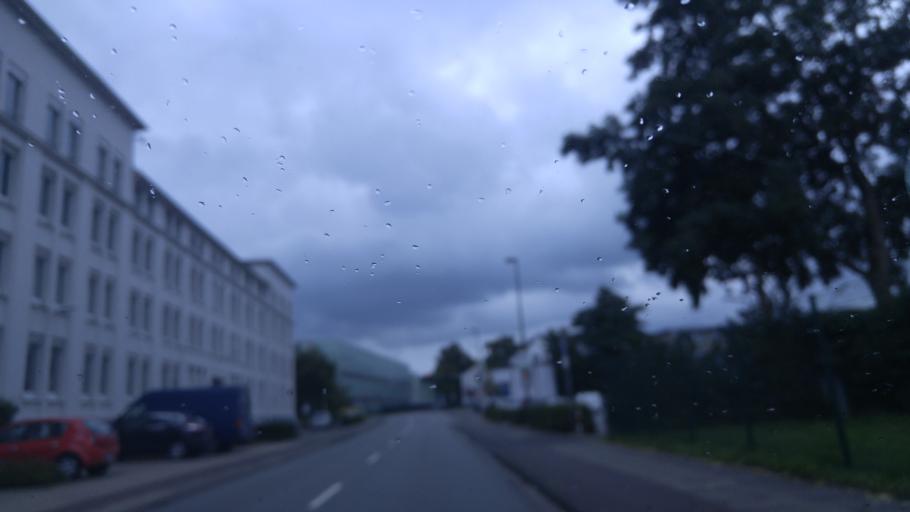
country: DE
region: North Rhine-Westphalia
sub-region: Regierungsbezirk Detmold
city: Bielefeld
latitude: 52.0383
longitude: 8.5379
